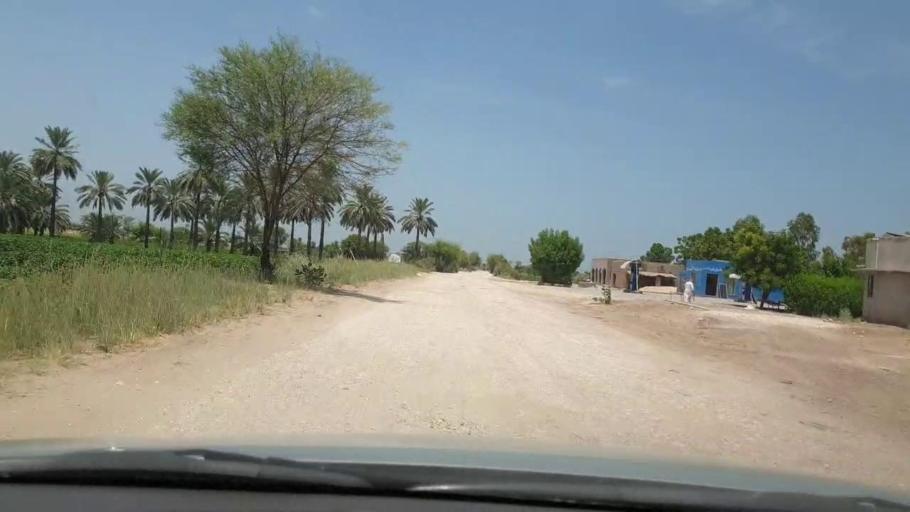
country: PK
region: Sindh
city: Pano Aqil
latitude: 27.6983
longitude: 69.2175
